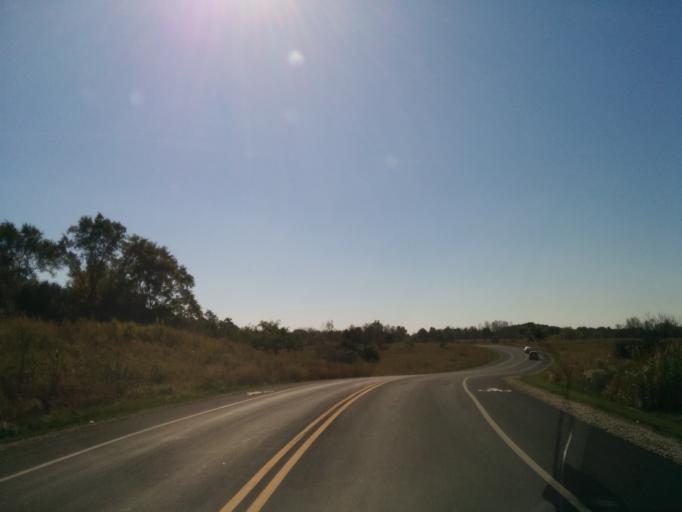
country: US
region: Illinois
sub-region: DuPage County
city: Hanover Park
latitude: 41.9598
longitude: -88.1277
